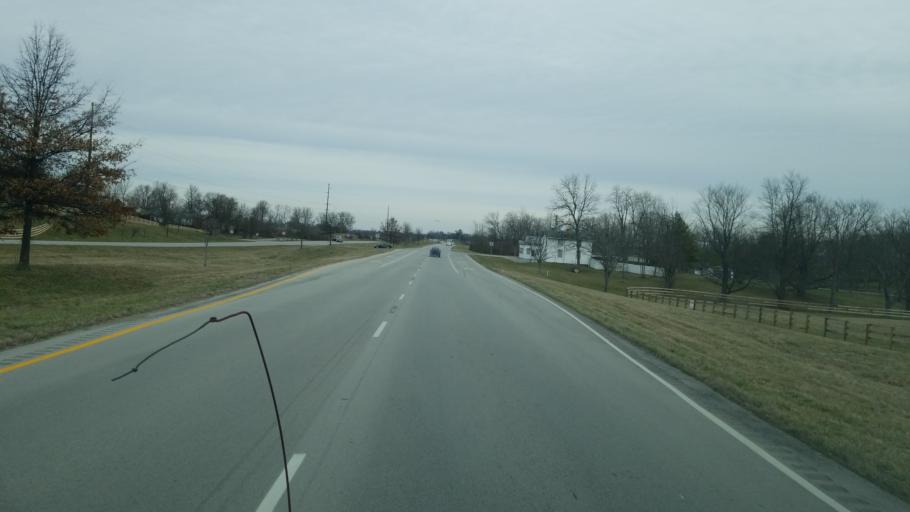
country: US
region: Kentucky
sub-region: Fayette County
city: Lexington-Fayette
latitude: 38.1345
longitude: -84.3672
